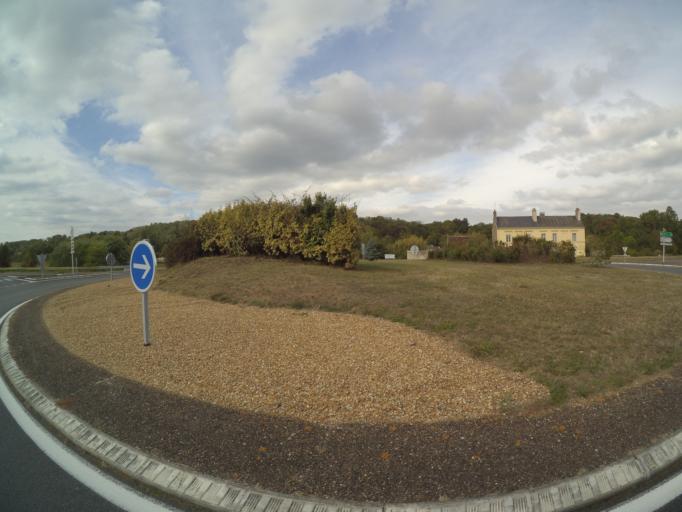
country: FR
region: Centre
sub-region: Departement d'Indre-et-Loire
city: Cinq-Mars-la-Pile
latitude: 47.3509
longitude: 0.4783
